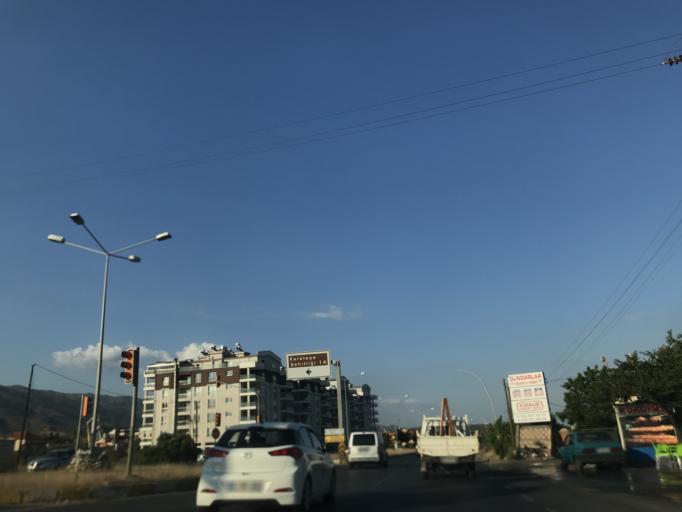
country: TR
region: Aydin
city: Kosk
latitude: 37.8529
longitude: 28.0581
